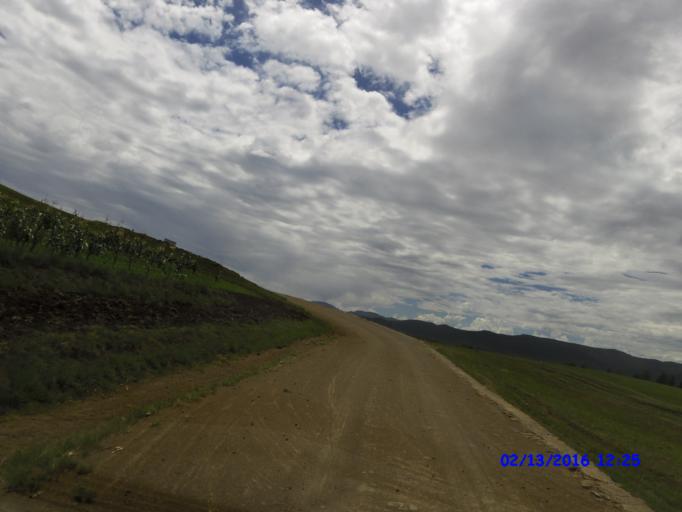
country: LS
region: Maseru
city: Nako
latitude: -29.8750
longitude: 28.0429
